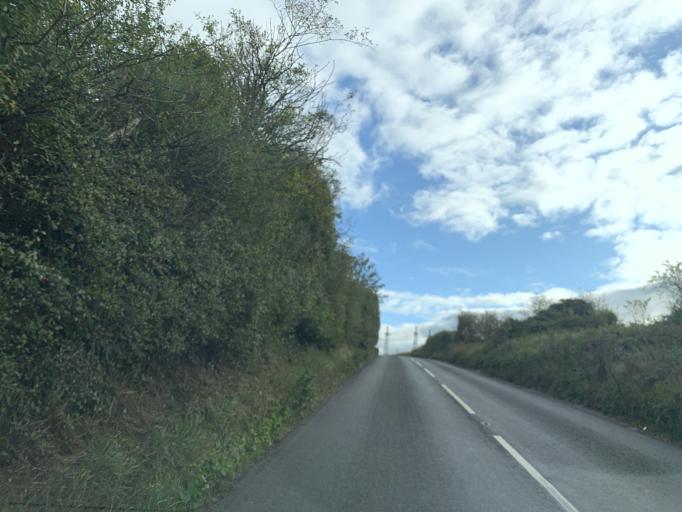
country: GB
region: England
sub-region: Wiltshire
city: Bulford
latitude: 51.1864
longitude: -1.7610
